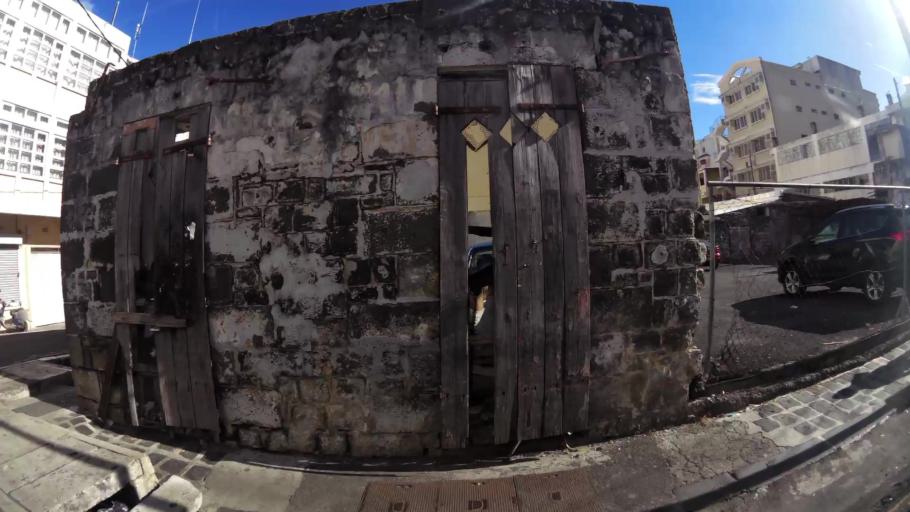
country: MU
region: Port Louis
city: Port Louis
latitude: -20.1608
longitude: 57.5071
